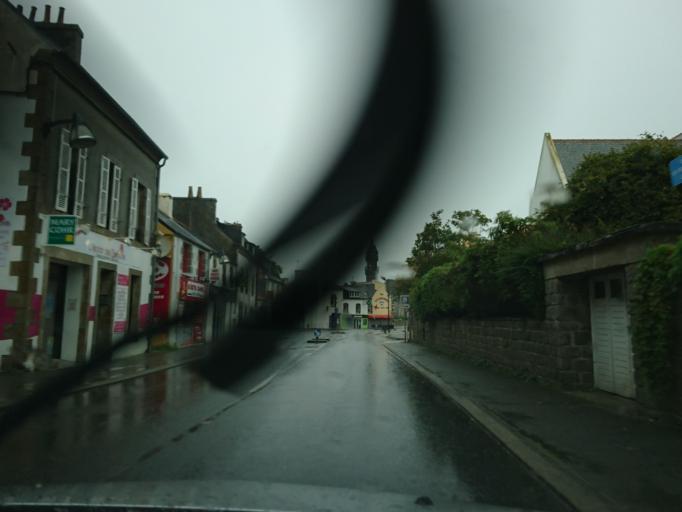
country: FR
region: Brittany
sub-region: Departement du Finistere
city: Plabennec
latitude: 48.5007
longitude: -4.4271
